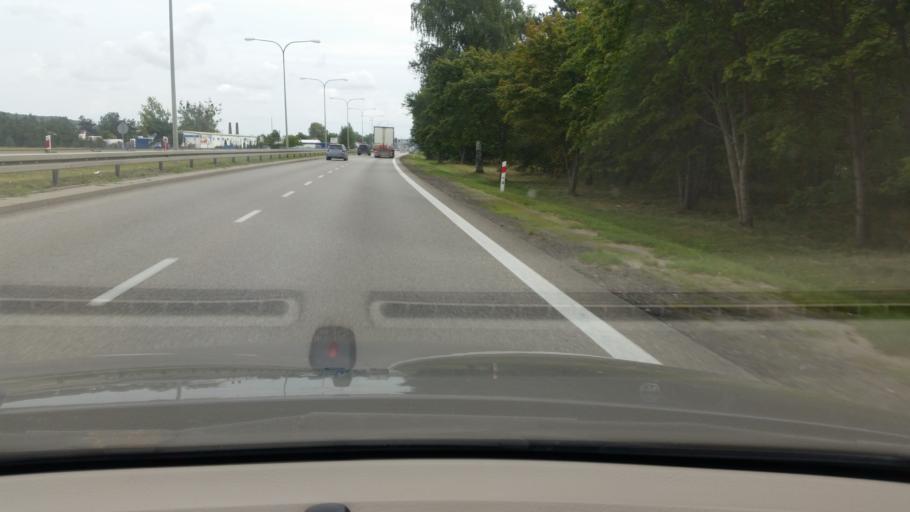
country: PL
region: Pomeranian Voivodeship
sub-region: Powiat wejherowski
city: Bolszewo
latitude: 54.6104
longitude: 18.1922
